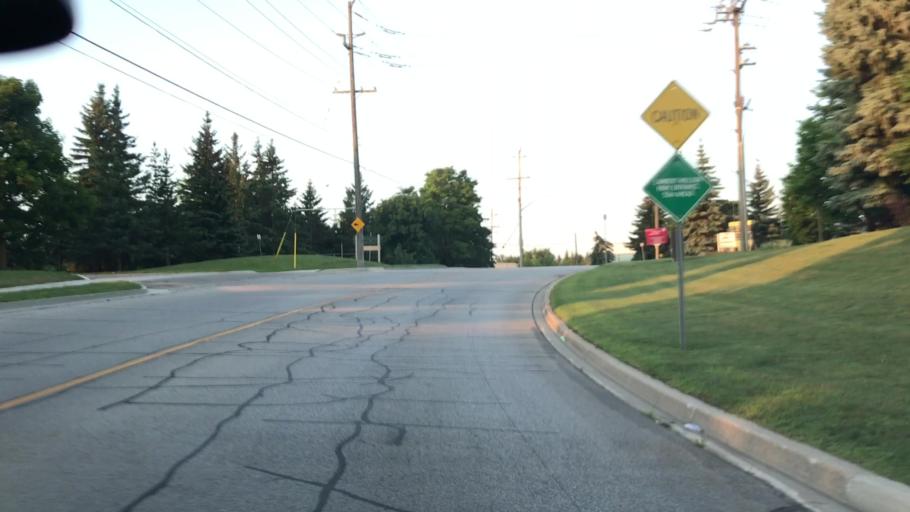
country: CA
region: Ontario
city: Newmarket
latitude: 44.0111
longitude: -79.4612
